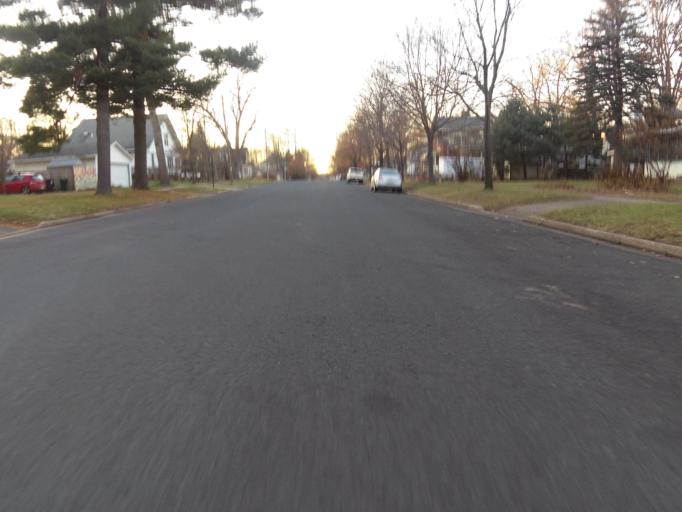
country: US
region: Wisconsin
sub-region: Pierce County
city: River Falls
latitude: 44.8582
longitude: -92.6200
